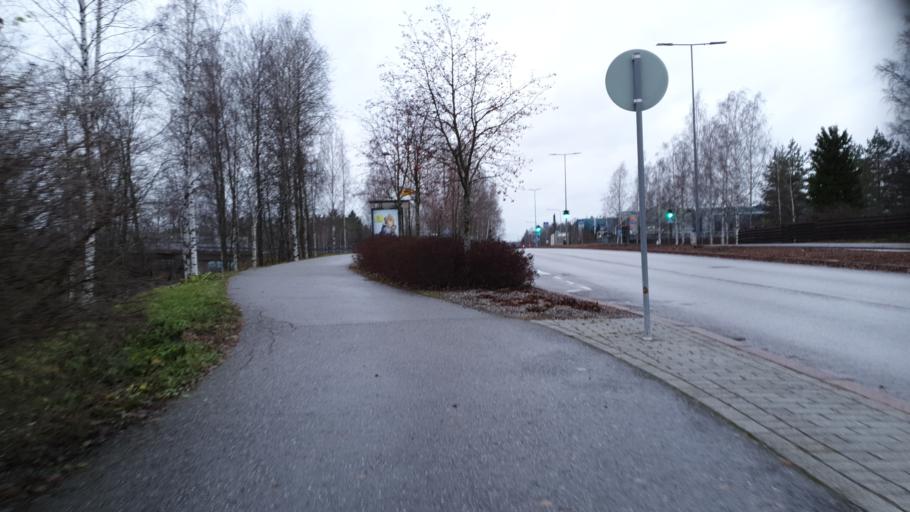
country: FI
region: Uusimaa
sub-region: Helsinki
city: Teekkarikylae
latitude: 60.2819
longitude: 24.8527
